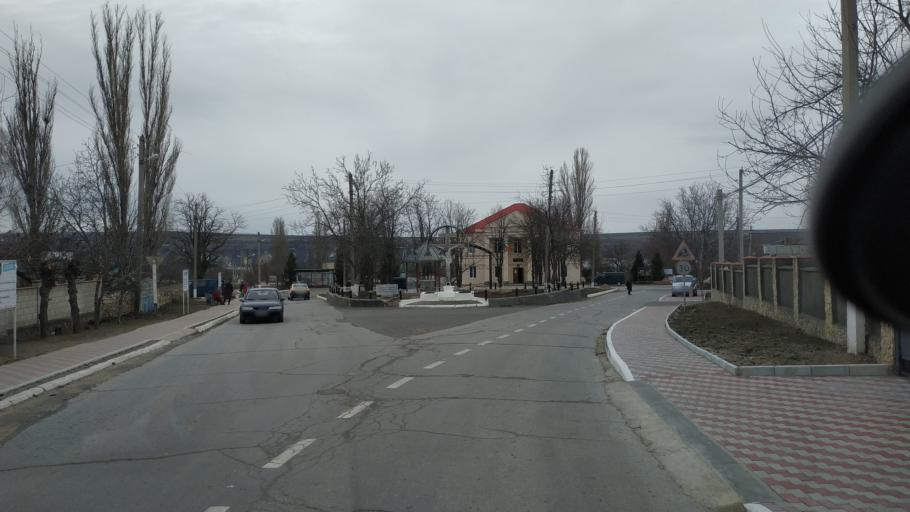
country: MD
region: Telenesti
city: Cocieri
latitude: 47.3461
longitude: 29.0910
